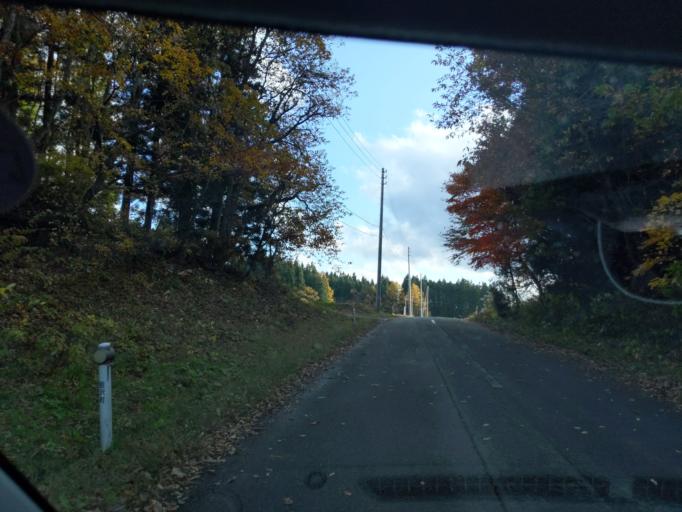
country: JP
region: Iwate
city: Mizusawa
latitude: 39.1209
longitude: 140.9763
